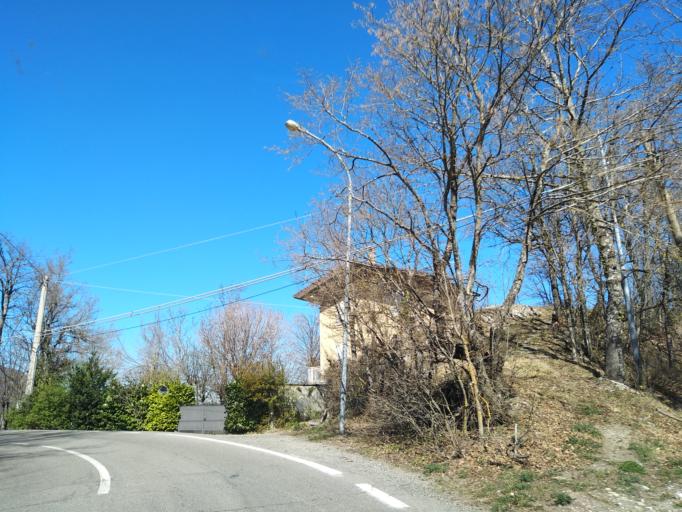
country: IT
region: Emilia-Romagna
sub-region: Provincia di Reggio Emilia
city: Ramiseto
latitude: 44.4157
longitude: 10.2974
